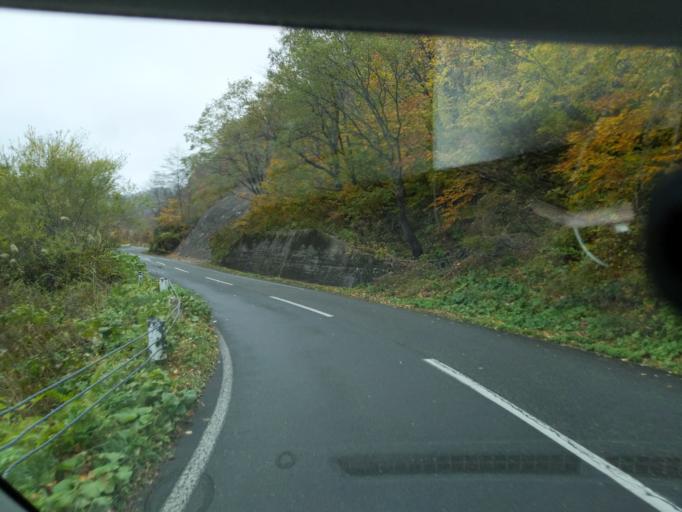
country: JP
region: Iwate
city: Mizusawa
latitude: 39.1179
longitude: 140.8338
